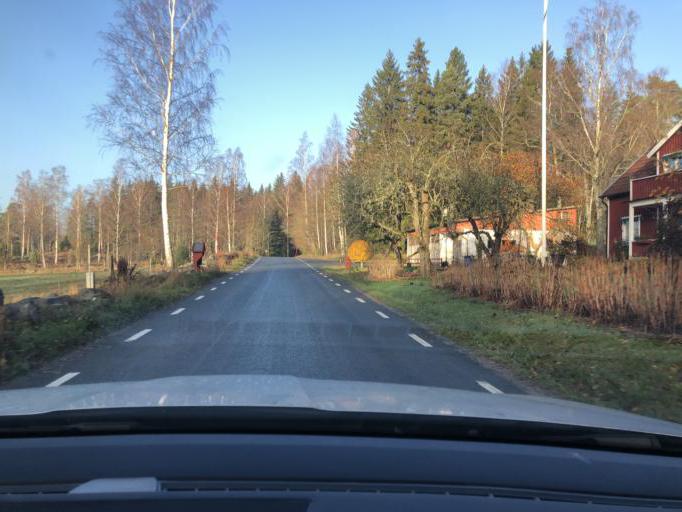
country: SE
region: Soedermanland
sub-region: Flens Kommun
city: Halleforsnas
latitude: 59.1130
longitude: 16.4400
